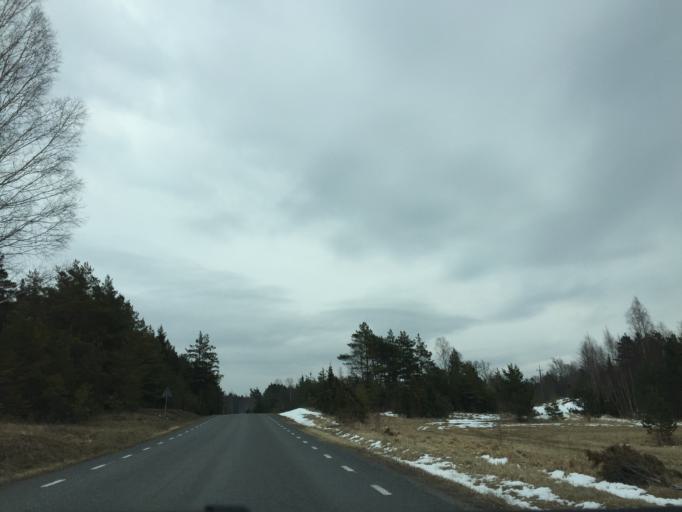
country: EE
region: Saare
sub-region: Kuressaare linn
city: Kuressaare
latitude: 58.4172
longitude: 22.1340
